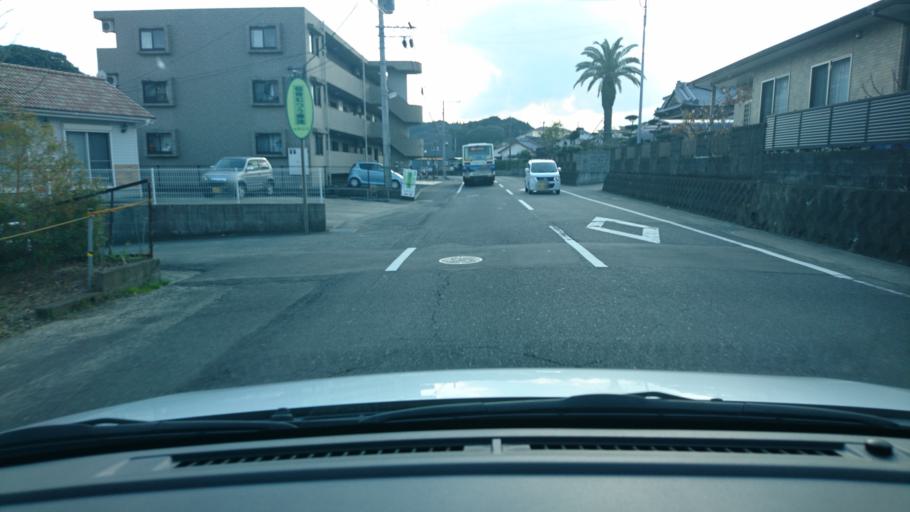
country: JP
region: Miyazaki
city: Miyazaki-shi
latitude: 31.8713
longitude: 131.4043
